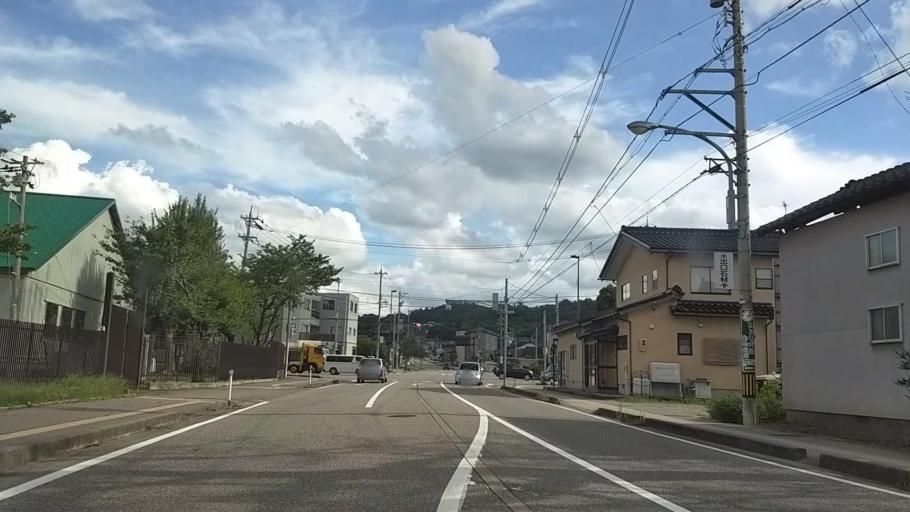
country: JP
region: Ishikawa
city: Nonoichi
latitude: 36.5369
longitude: 136.6674
